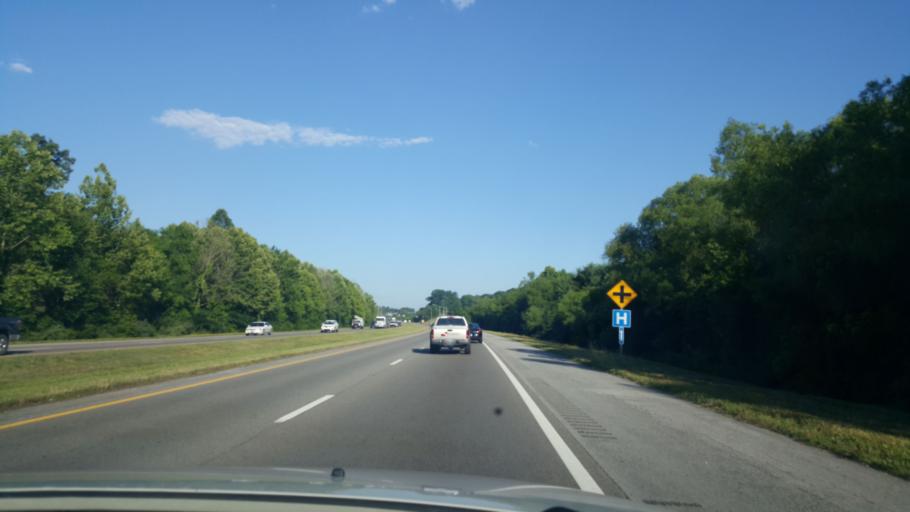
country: US
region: Tennessee
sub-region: Maury County
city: Columbia
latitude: 35.6371
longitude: -87.0226
